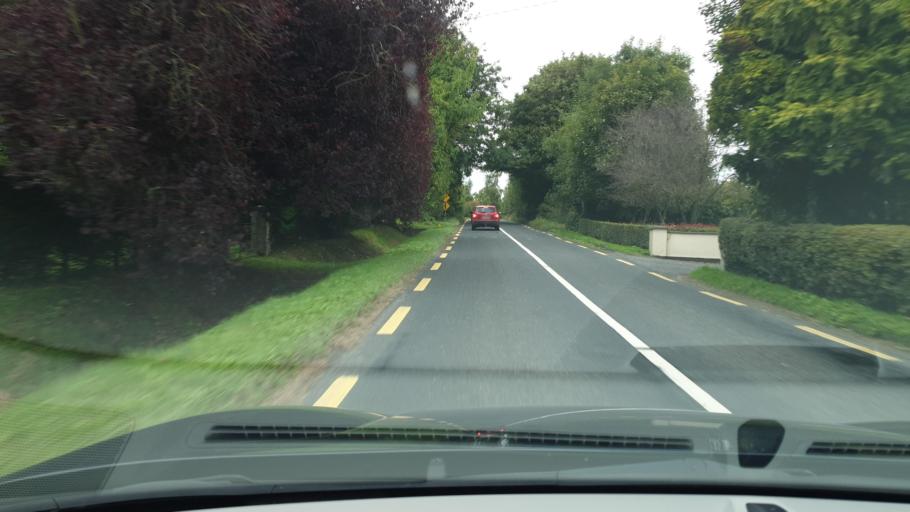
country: IE
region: Leinster
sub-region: Kildare
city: Clane
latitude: 53.2671
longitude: -6.6855
